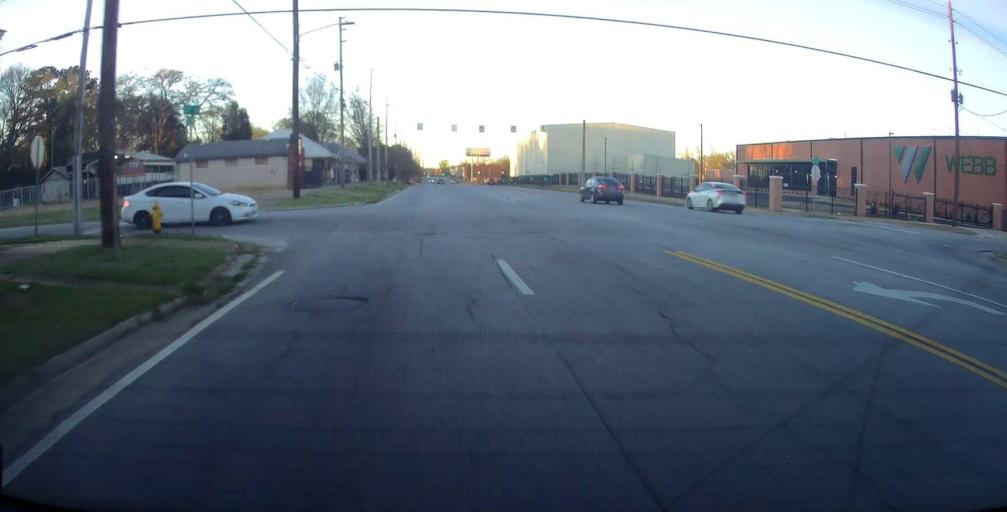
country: US
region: Alabama
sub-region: Russell County
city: Phenix City
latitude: 32.4935
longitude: -84.9902
